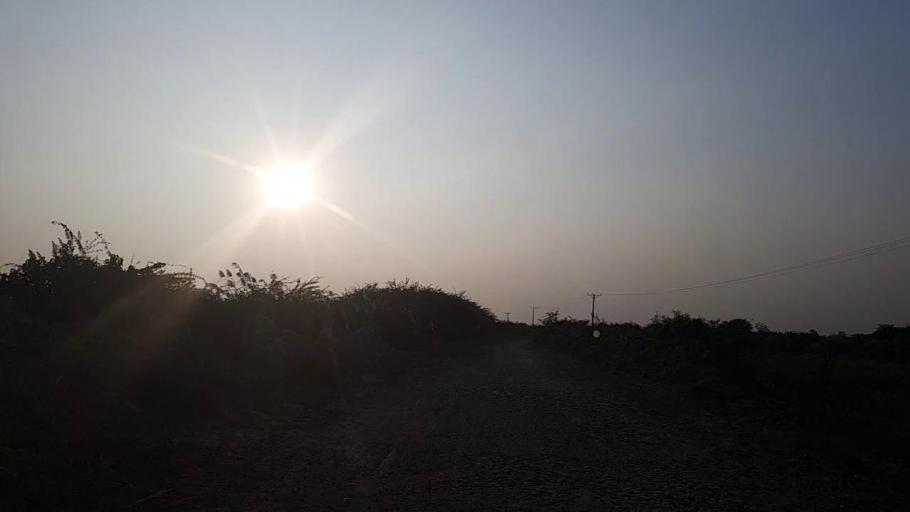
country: PK
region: Sindh
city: Mirpur Sakro
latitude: 24.5544
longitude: 67.5746
